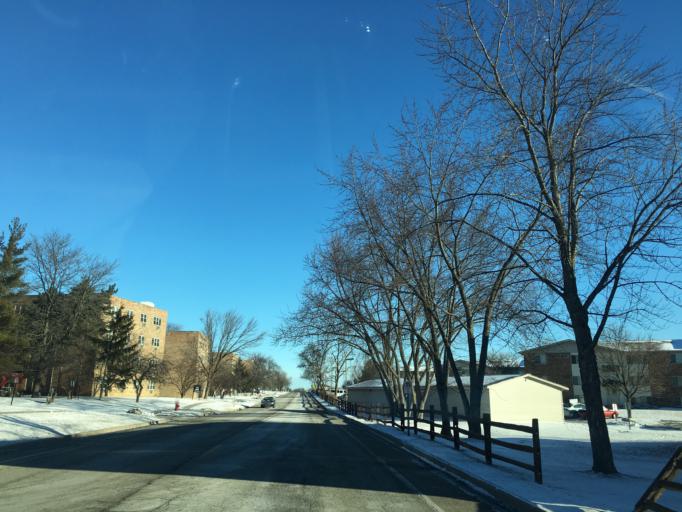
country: US
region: Illinois
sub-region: Cook County
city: Schaumburg
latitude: 42.0377
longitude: -88.1019
